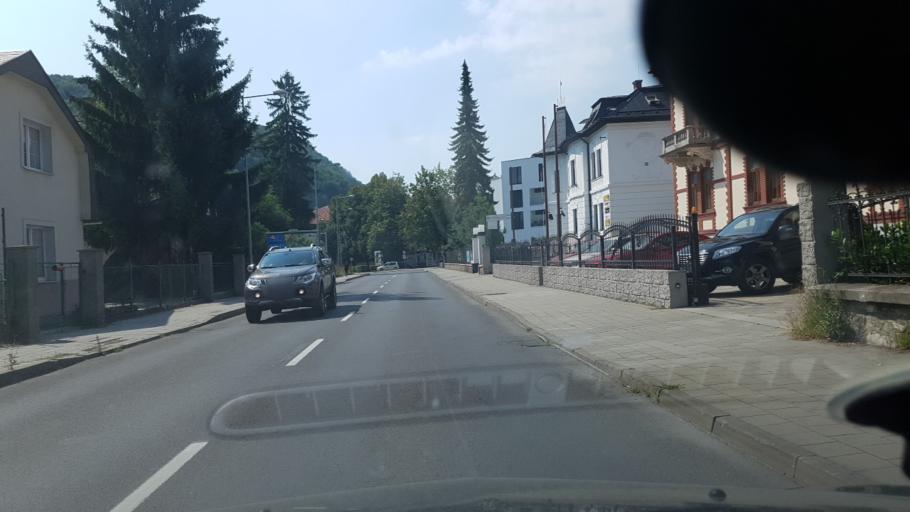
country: SK
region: Banskobystricky
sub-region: Okres Banska Bystrica
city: Banska Bystrica
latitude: 48.7345
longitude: 19.1391
